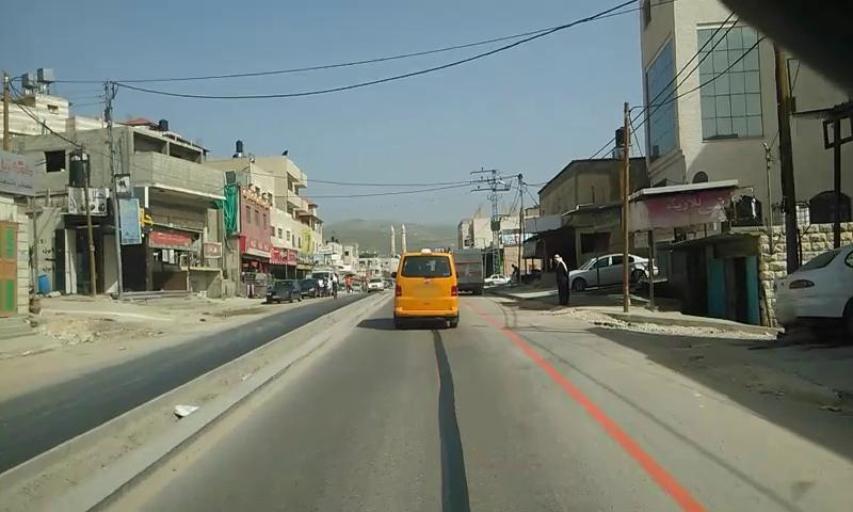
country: PS
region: West Bank
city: Huwwarah
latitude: 32.1524
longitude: 35.2589
